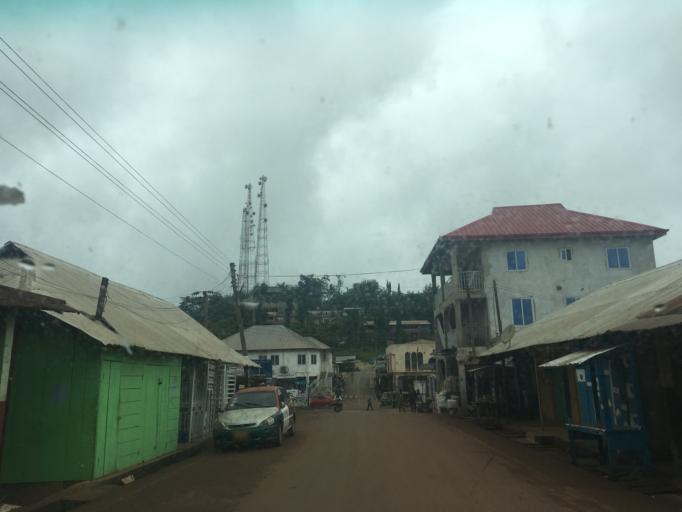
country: GH
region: Western
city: Wassa-Akropong
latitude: 5.8095
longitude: -2.4366
